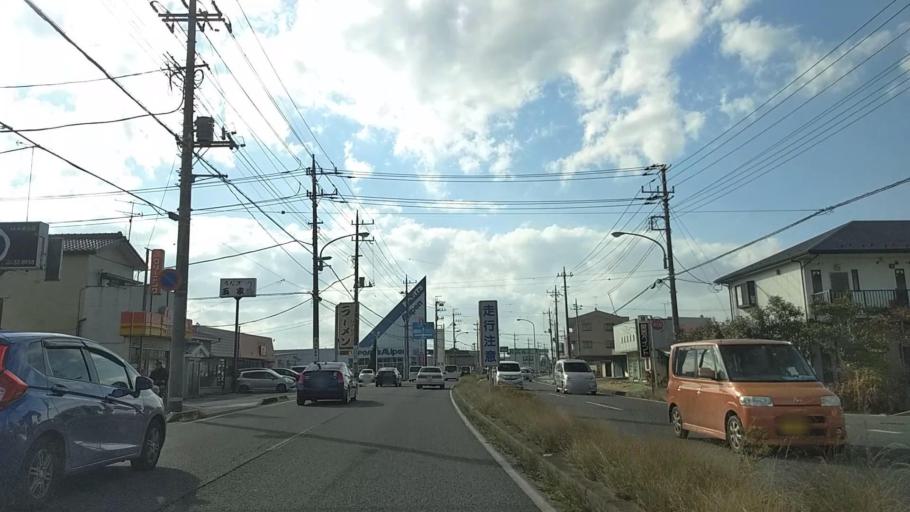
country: JP
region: Chiba
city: Togane
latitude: 35.5519
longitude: 140.3632
